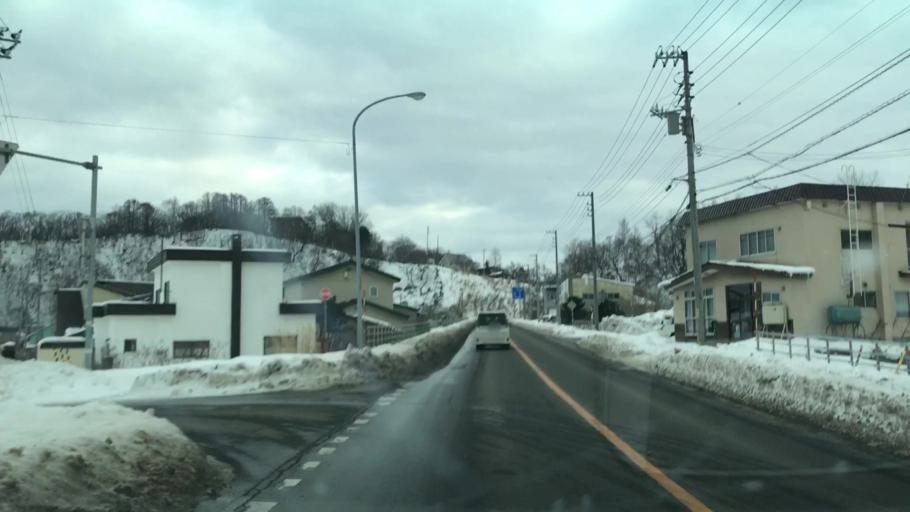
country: JP
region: Hokkaido
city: Yoichi
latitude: 43.1991
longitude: 140.7827
